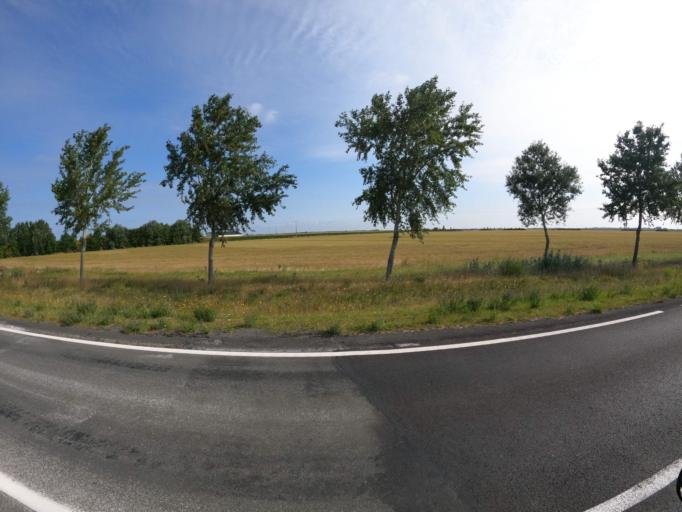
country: FR
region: Pays de la Loire
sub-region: Departement de la Vendee
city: Angles
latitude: 46.3457
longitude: -1.3121
